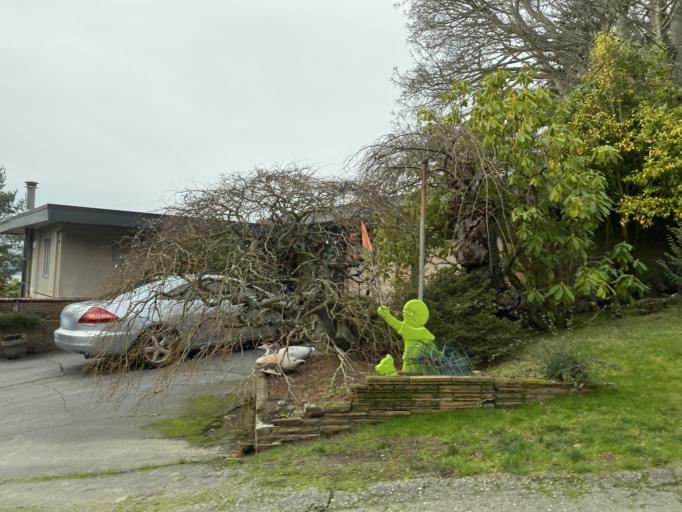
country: US
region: Washington
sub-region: King County
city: Seattle
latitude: 47.6451
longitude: -122.4167
